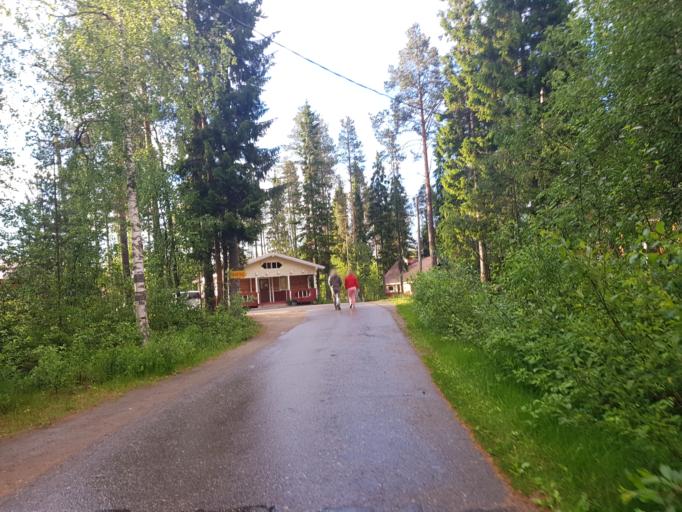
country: RU
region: Republic of Karelia
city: Kostomuksha
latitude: 64.6012
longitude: 30.5745
